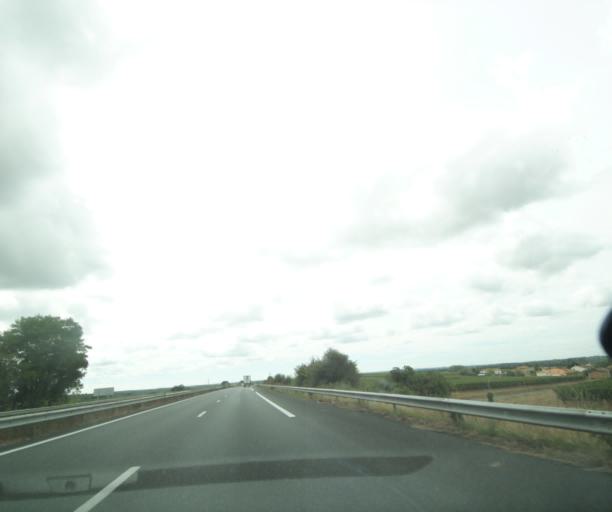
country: FR
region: Aquitaine
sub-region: Departement de la Gironde
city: Marcillac
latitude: 45.2878
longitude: -0.5518
